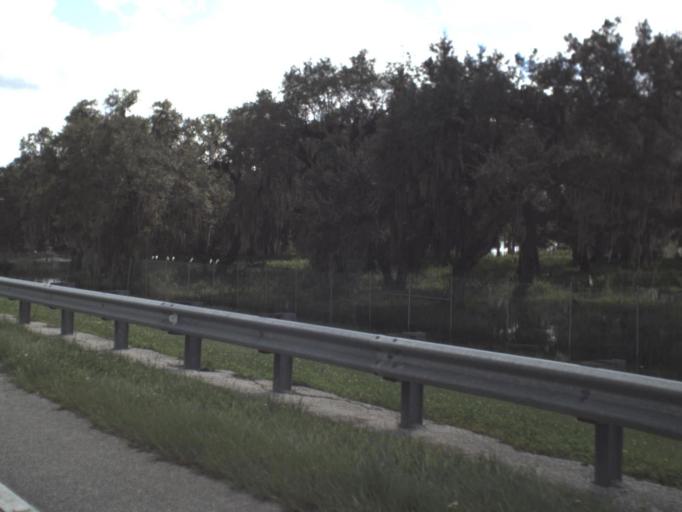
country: US
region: Florida
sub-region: DeSoto County
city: Arcadia
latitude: 27.2561
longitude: -81.9697
